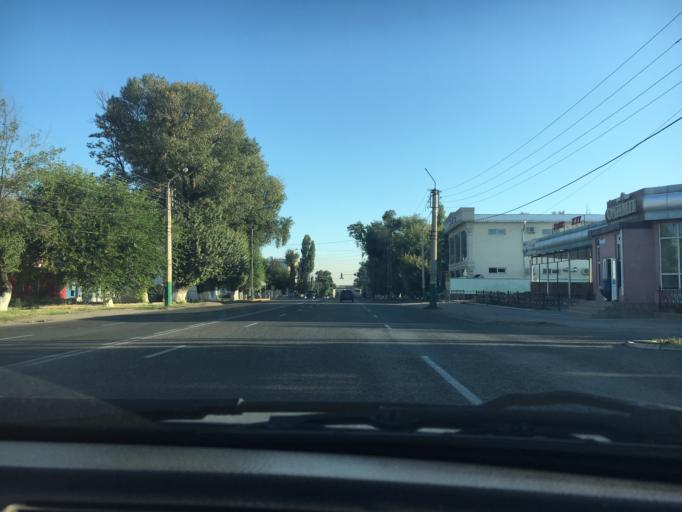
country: KZ
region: Zhambyl
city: Taraz
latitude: 42.8957
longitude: 71.3604
